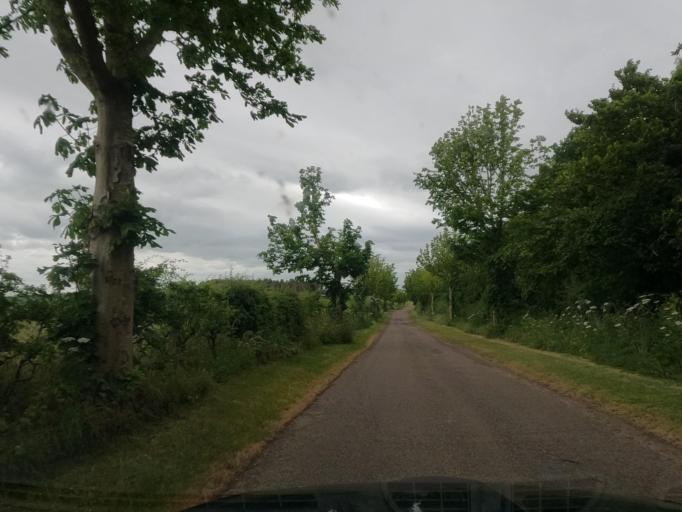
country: GB
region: England
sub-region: Northumberland
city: Ford
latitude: 55.6767
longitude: -2.1065
